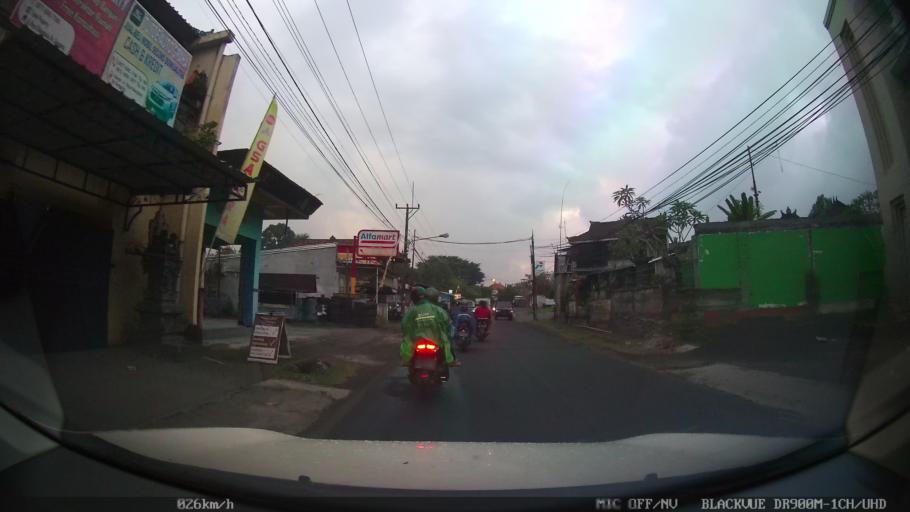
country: ID
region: Bali
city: Banjar Mambalkajanan
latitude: -8.5619
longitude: 115.2203
